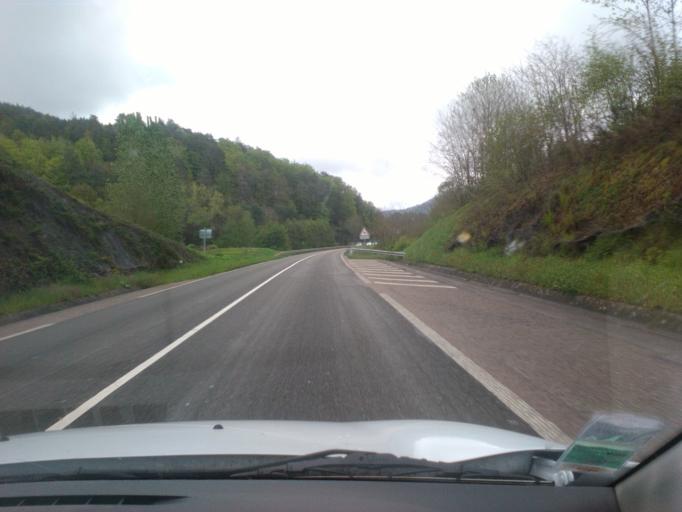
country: FR
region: Lorraine
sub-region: Departement des Vosges
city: Saint-Etienne-les-Remiremont
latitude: 48.0158
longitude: 6.6208
